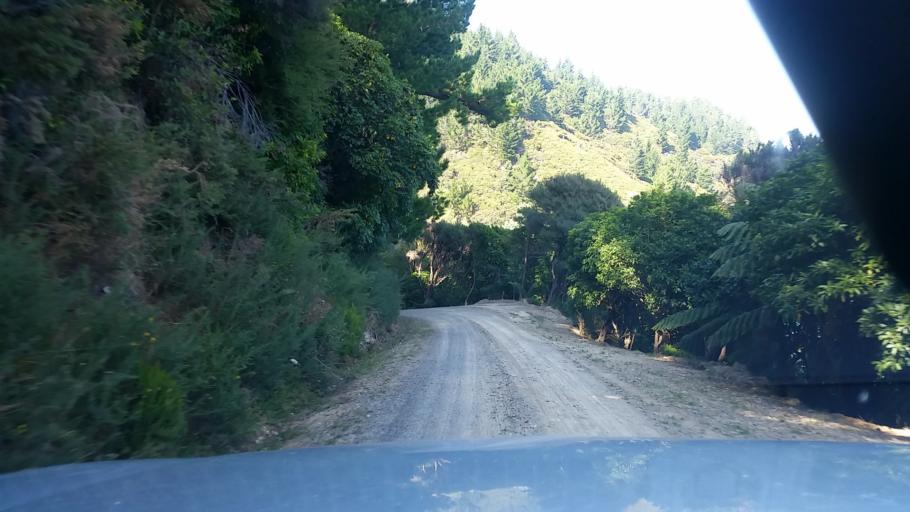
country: NZ
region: Marlborough
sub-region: Marlborough District
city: Picton
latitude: -41.3020
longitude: 174.1782
